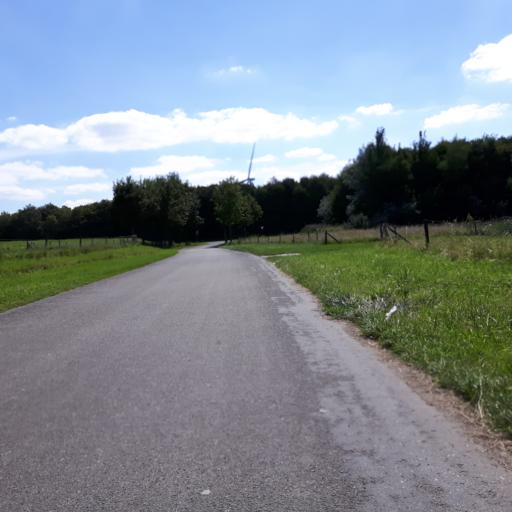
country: NL
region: North Brabant
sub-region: Gemeente Woensdrecht
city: Woensdrecht
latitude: 51.4311
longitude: 4.2375
